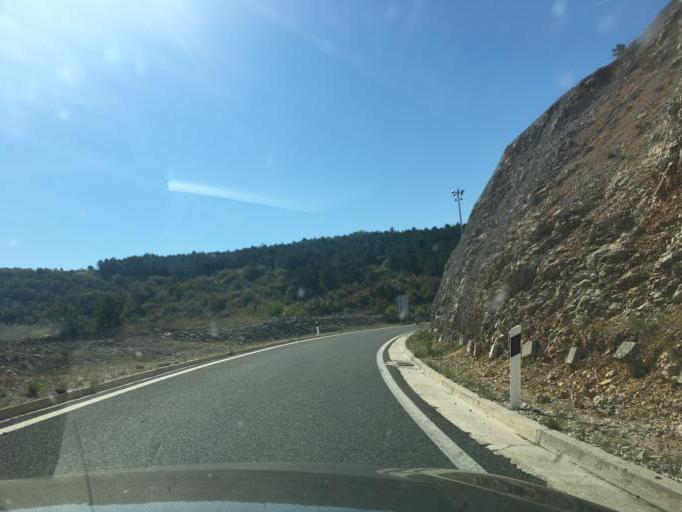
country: HR
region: Splitsko-Dalmatinska
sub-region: Grad Trogir
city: Trogir
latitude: 43.6219
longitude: 16.2417
